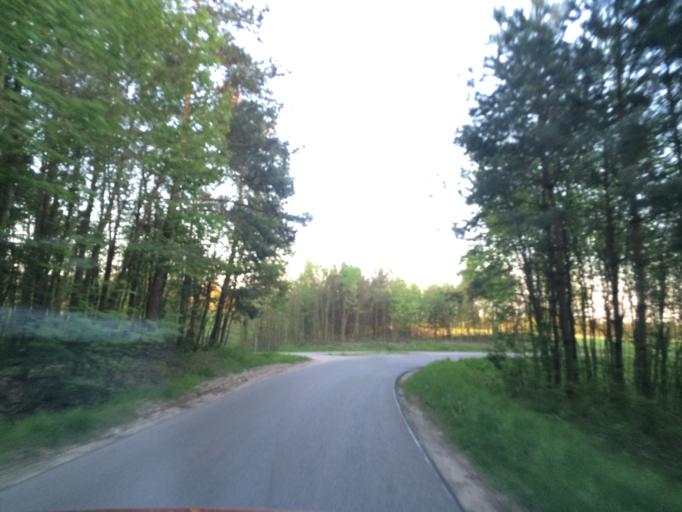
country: PL
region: Warmian-Masurian Voivodeship
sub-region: Powiat dzialdowski
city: Rybno
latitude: 53.4348
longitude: 19.9200
